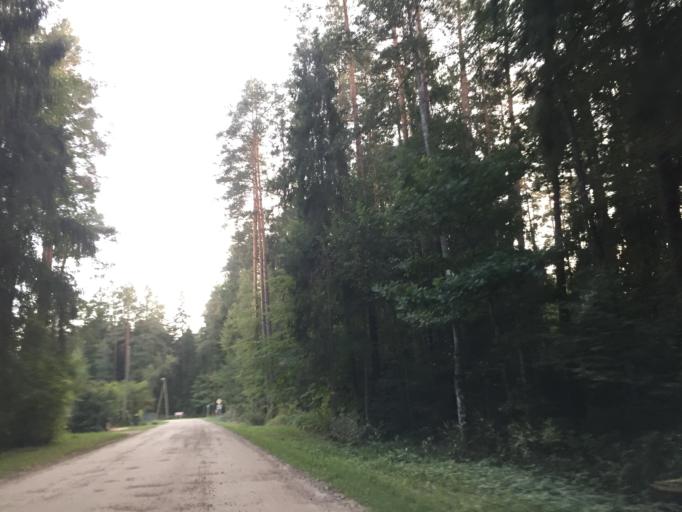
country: LV
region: Baldone
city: Baldone
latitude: 56.7524
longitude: 24.4043
